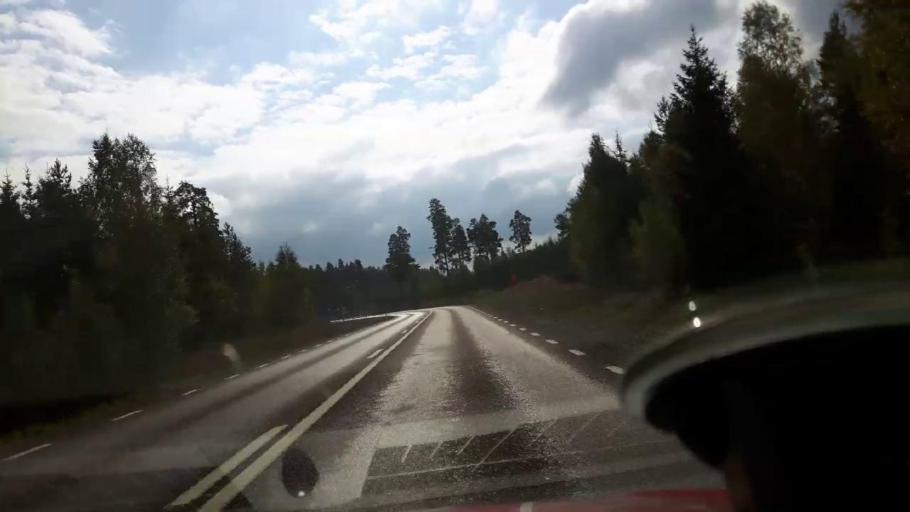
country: SE
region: Gaevleborg
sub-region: Gavle Kommun
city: Norrsundet
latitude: 61.0752
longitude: 16.9628
